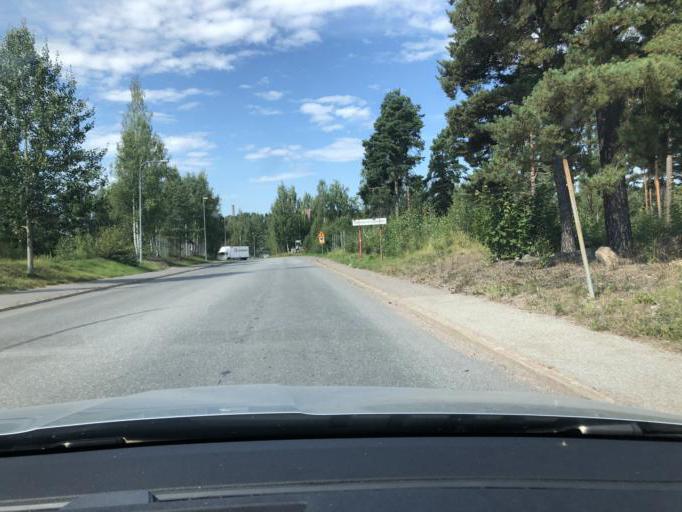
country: SE
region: Dalarna
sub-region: Avesta Kommun
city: Avesta
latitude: 60.1450
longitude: 16.1934
